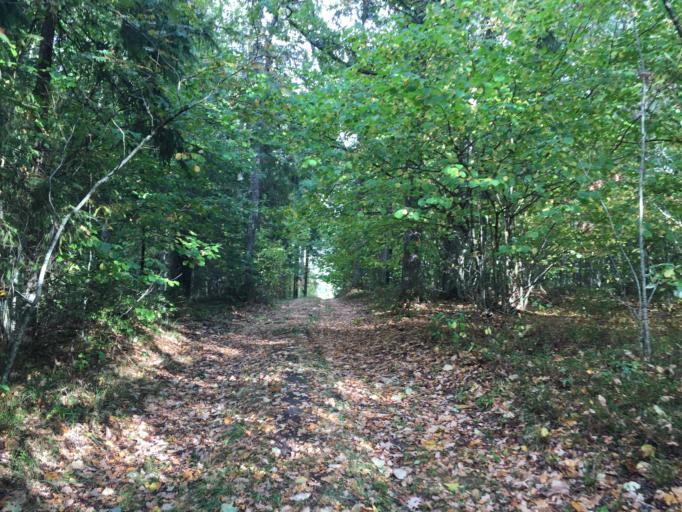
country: LV
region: Ligatne
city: Ligatne
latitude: 57.1149
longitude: 25.1374
